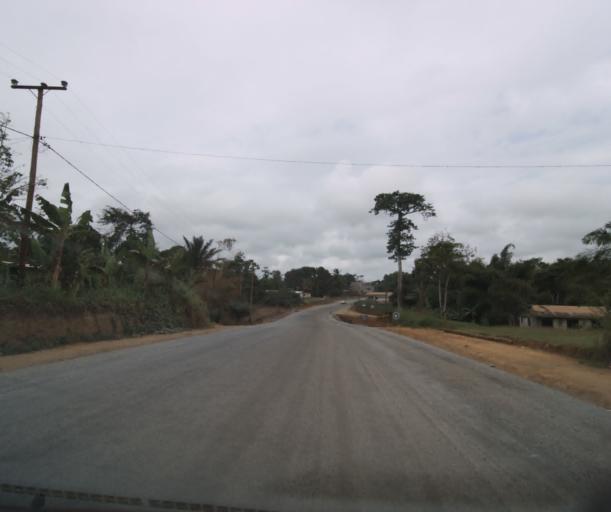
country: CM
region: South Province
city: Kribi
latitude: 2.9079
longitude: 9.9047
